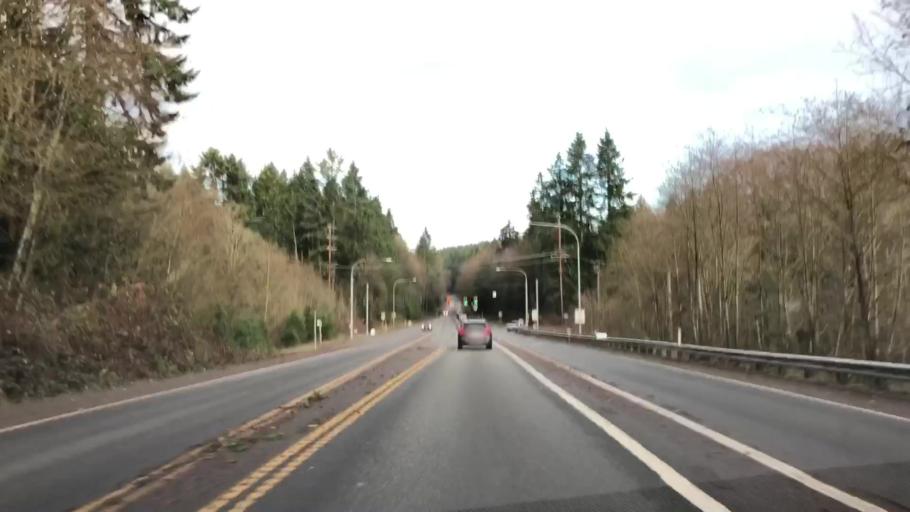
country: US
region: Washington
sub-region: Kitsap County
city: Bainbridge Island
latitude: 47.6525
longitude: -122.5233
